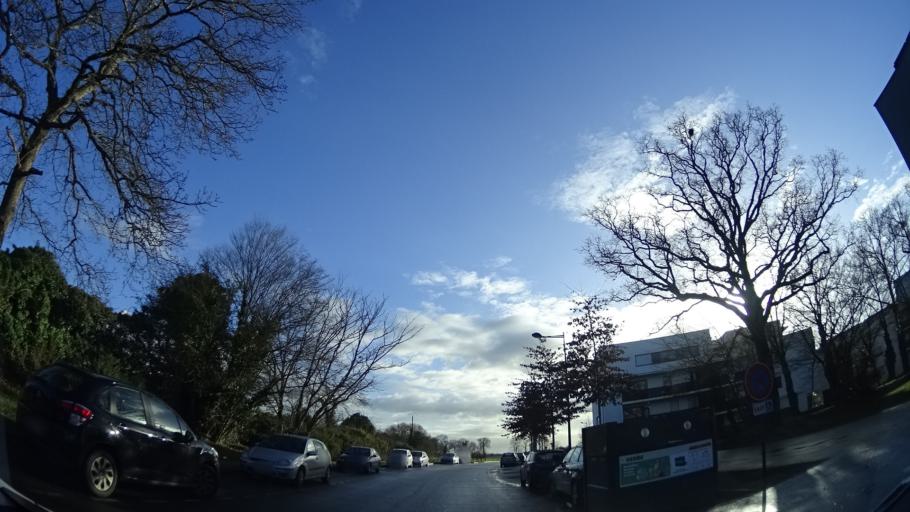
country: FR
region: Brittany
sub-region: Departement d'Ille-et-Vilaine
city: Chantepie
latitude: 48.0872
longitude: -1.6015
